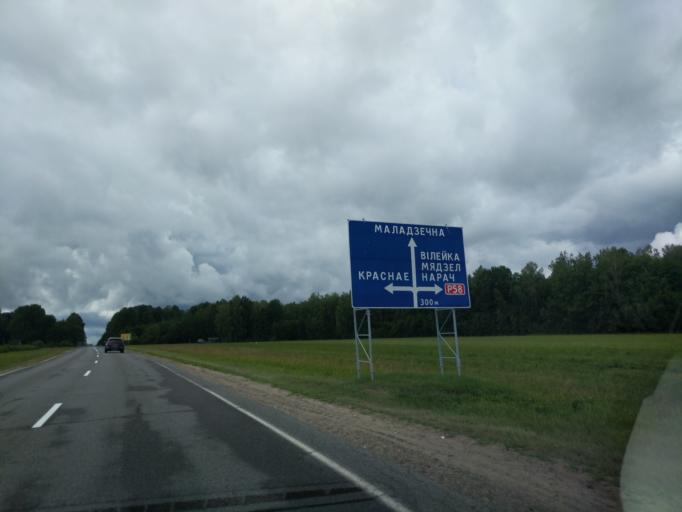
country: BY
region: Minsk
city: Il'ya
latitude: 54.4125
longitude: 27.2685
